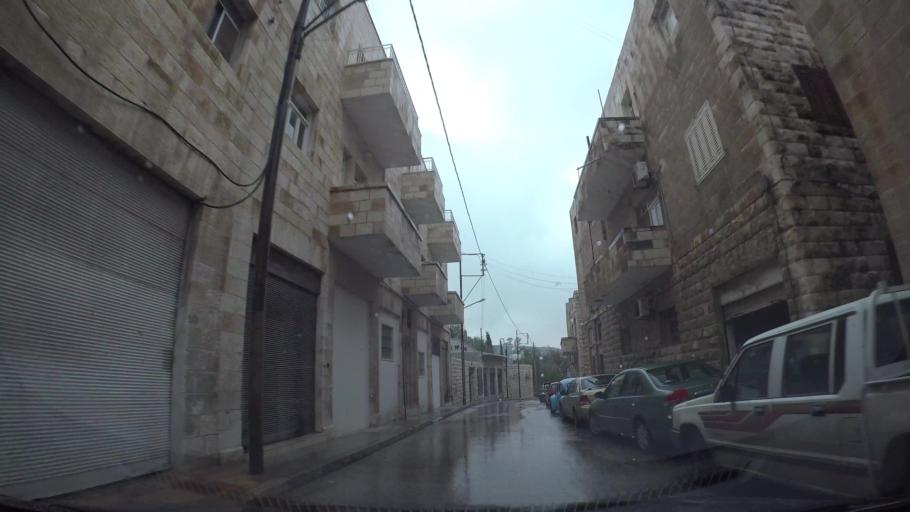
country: JO
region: Amman
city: Amman
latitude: 31.9538
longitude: 35.9296
